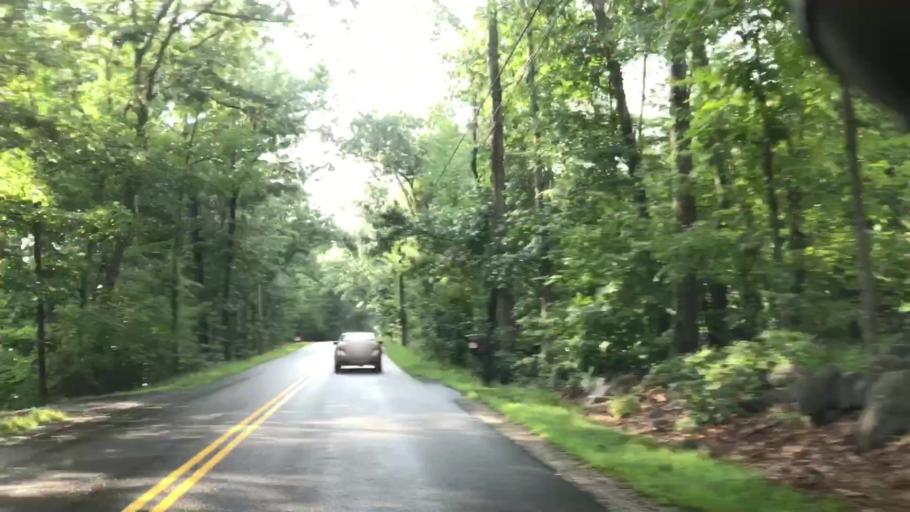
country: US
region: New Hampshire
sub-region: Hillsborough County
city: Milford
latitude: 42.8427
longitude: -71.6059
